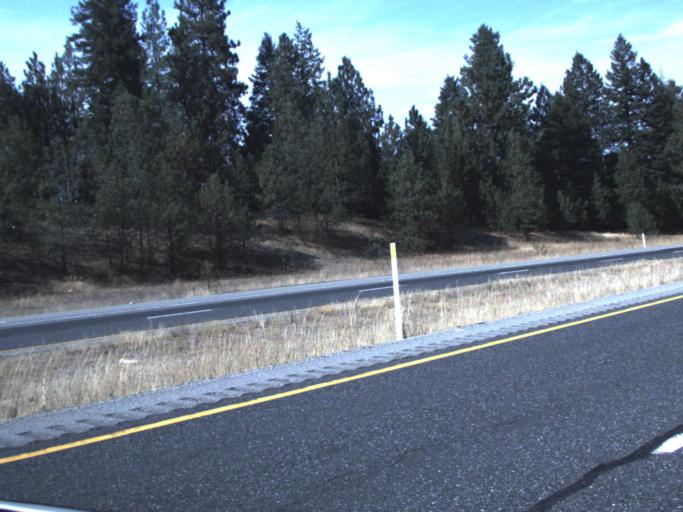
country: US
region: Washington
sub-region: Spokane County
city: Mead
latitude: 47.8829
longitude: -117.3574
